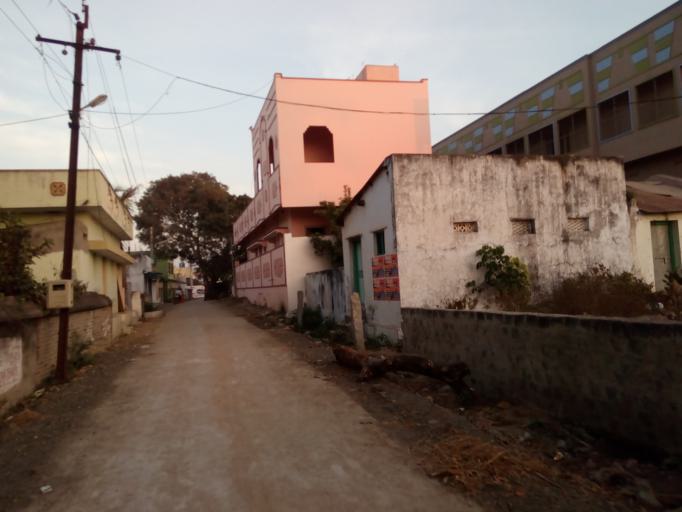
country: IN
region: Andhra Pradesh
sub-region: Prakasam
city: Vetapalem
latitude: 15.7273
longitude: 80.2525
